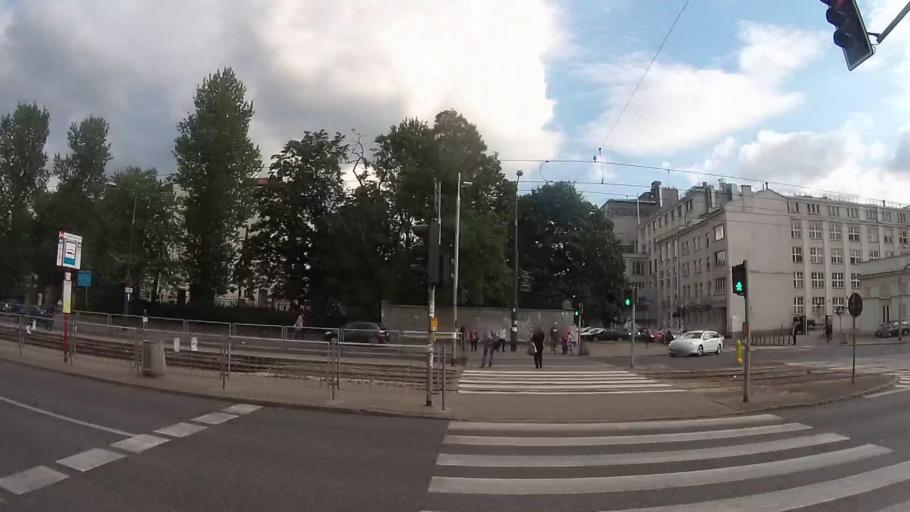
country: PL
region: Masovian Voivodeship
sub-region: Warszawa
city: Praga Polnoc
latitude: 52.2473
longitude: 21.0523
